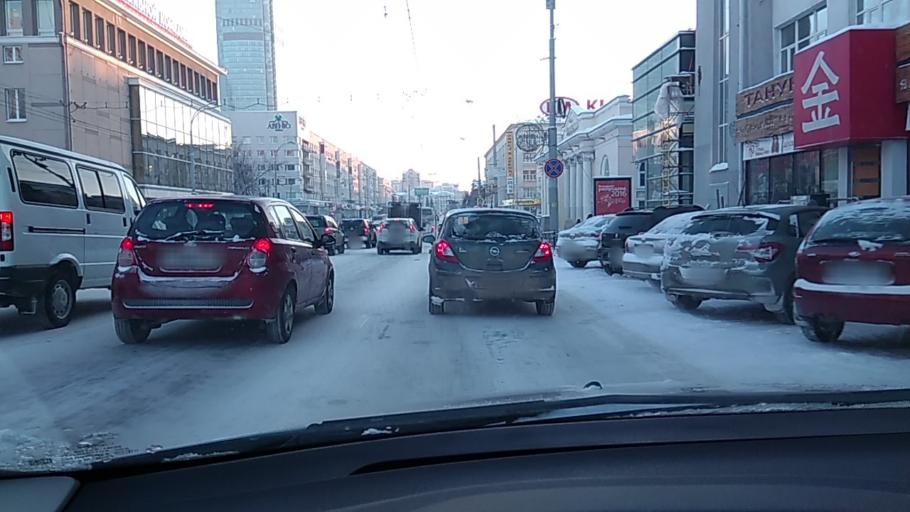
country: RU
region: Sverdlovsk
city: Yekaterinburg
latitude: 56.8403
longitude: 60.6109
